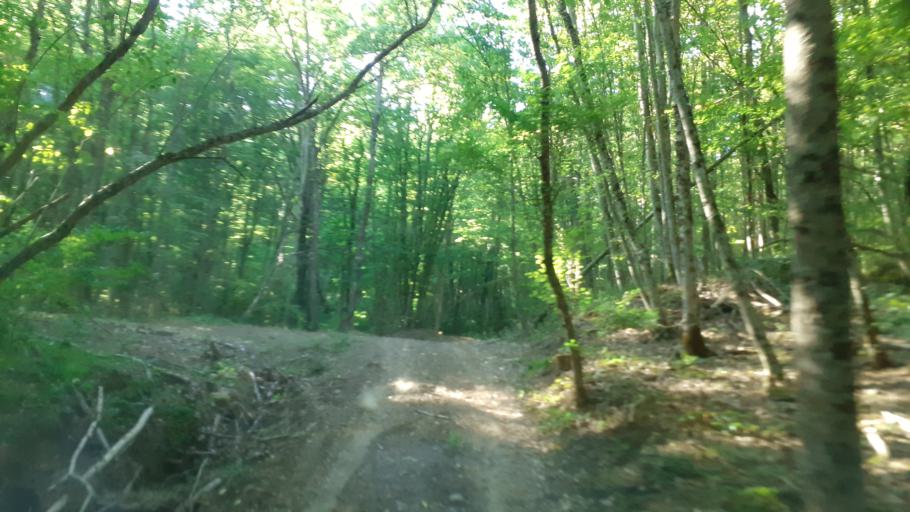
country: RU
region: Krasnodarskiy
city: Azovskaya
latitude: 44.6638
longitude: 38.4900
